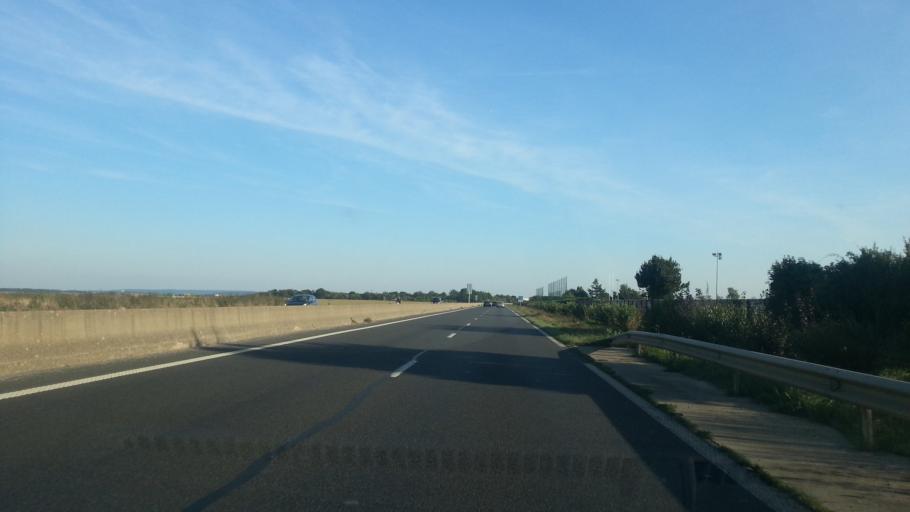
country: FR
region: Picardie
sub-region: Departement de l'Oise
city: Tille
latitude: 49.4471
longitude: 2.1058
